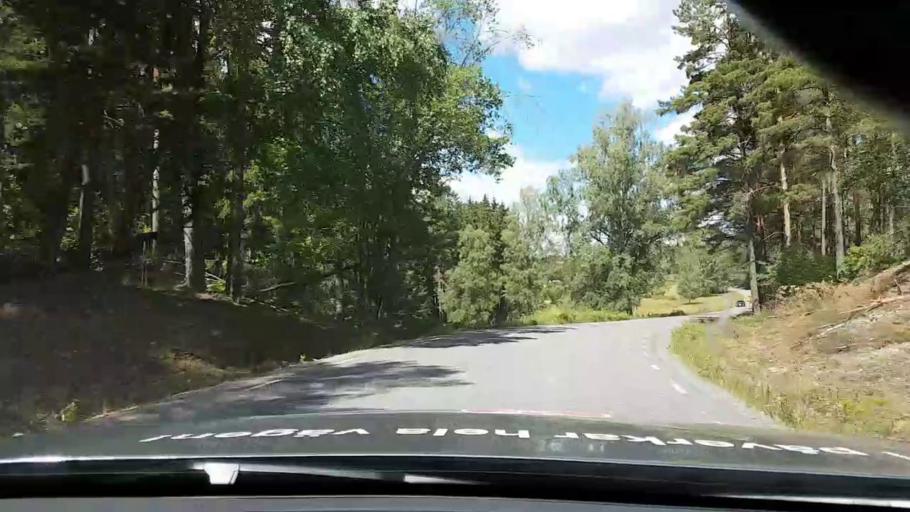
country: SE
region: Kalmar
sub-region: Vasterviks Kommun
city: Forserum
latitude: 58.0193
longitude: 16.5748
